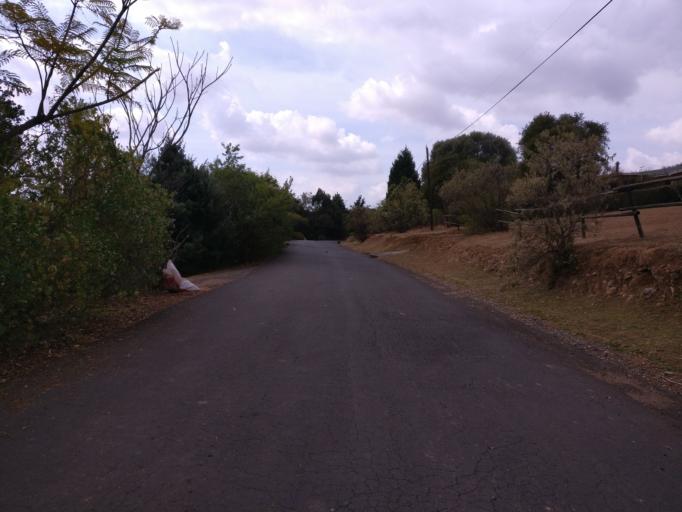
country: ZA
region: KwaZulu-Natal
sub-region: uThukela District Municipality
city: Bergville
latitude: -29.0137
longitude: 29.4163
